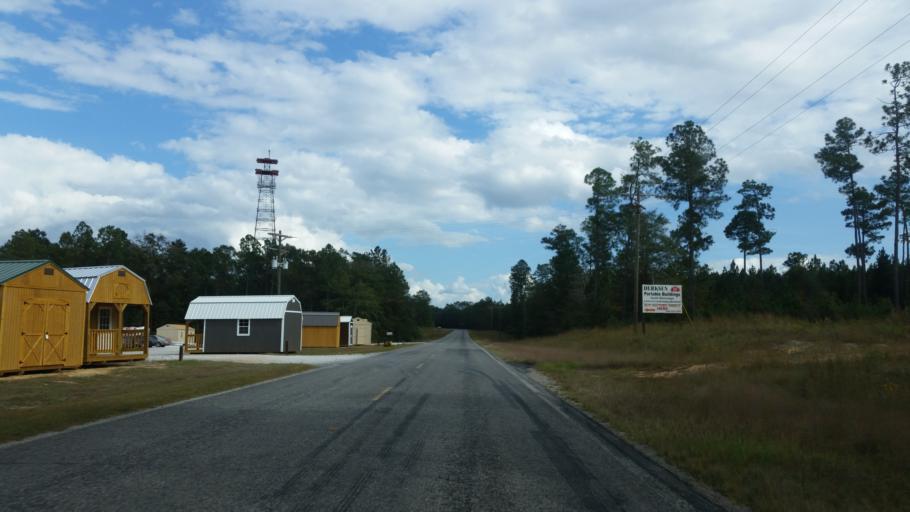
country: US
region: Mississippi
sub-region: Stone County
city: Wiggins
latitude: 30.9109
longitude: -89.0938
